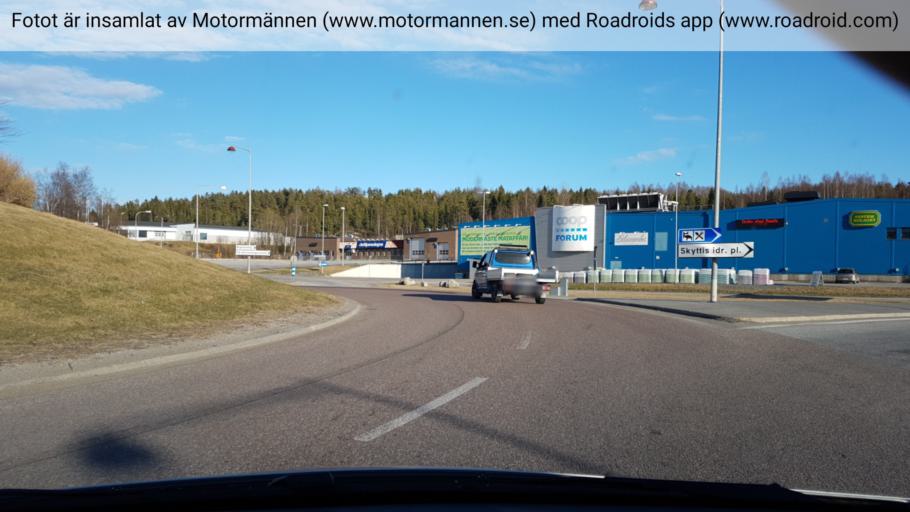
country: SE
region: Vaesternorrland
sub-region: OErnskoeldsviks Kommun
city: Ornskoldsvik
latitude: 63.3035
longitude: 18.7336
